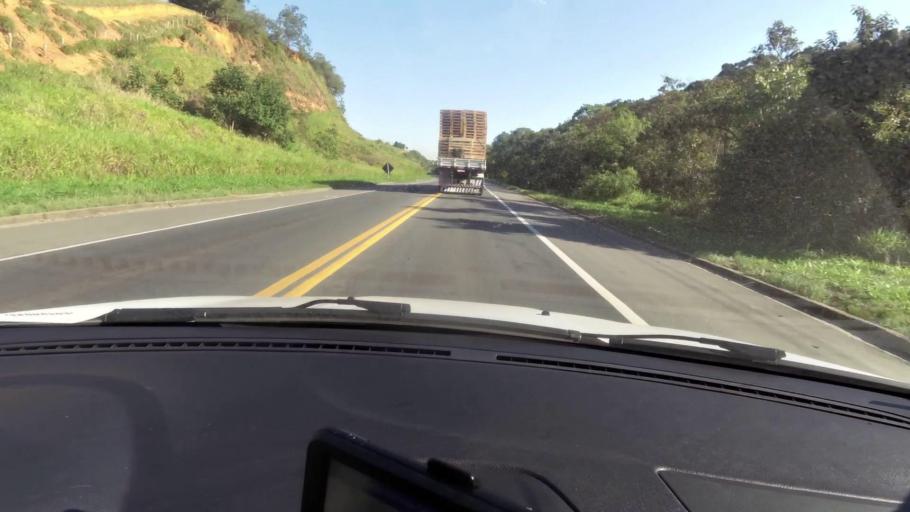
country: BR
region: Espirito Santo
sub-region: Alfredo Chaves
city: Alfredo Chaves
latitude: -20.6720
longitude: -40.6641
